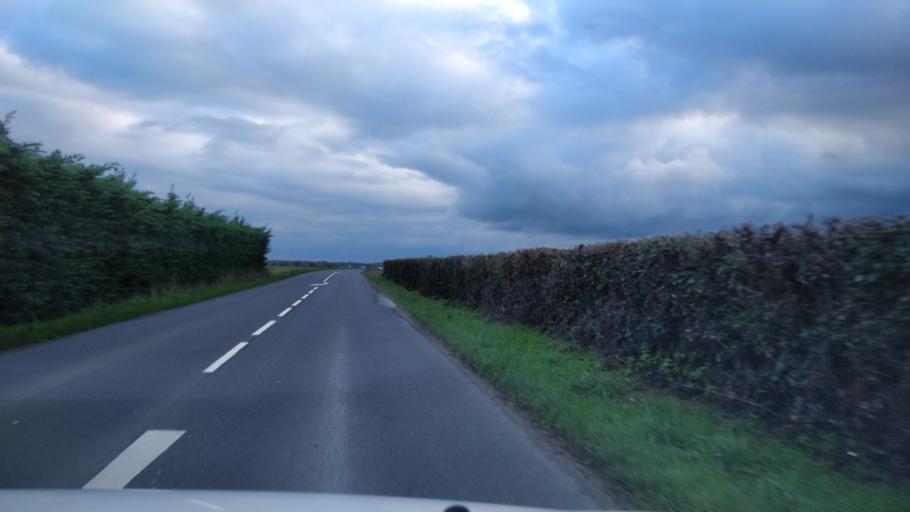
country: FR
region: Lower Normandy
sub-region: Departement du Calvados
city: Benouville
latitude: 49.2581
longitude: -0.2841
